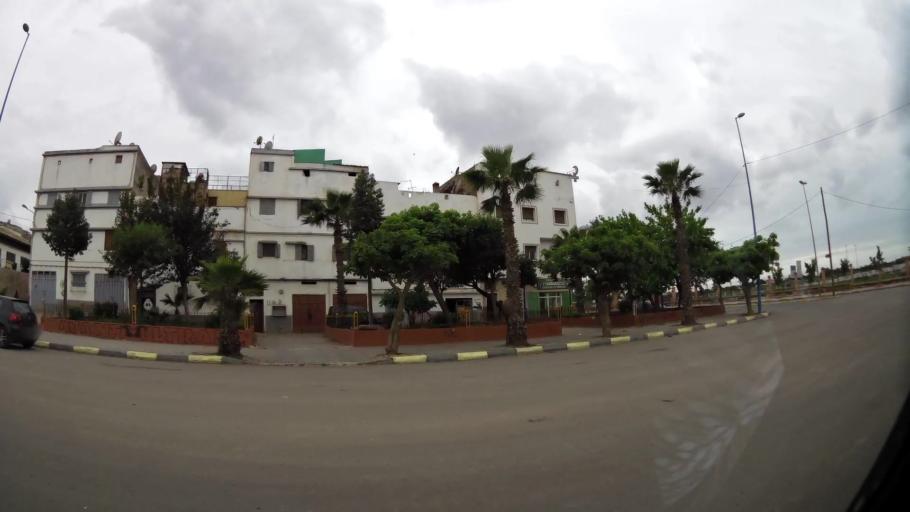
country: MA
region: Grand Casablanca
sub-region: Casablanca
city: Casablanca
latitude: 33.5702
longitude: -7.5672
